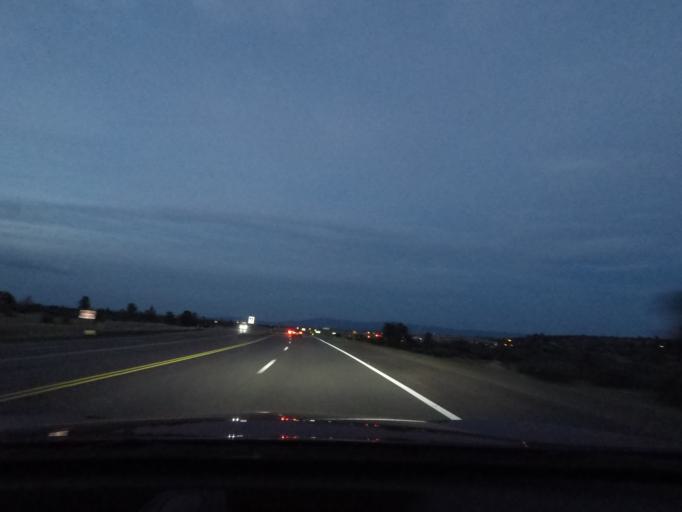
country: US
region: Arizona
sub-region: Yavapai County
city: Prescott
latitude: 34.6298
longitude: -112.4350
